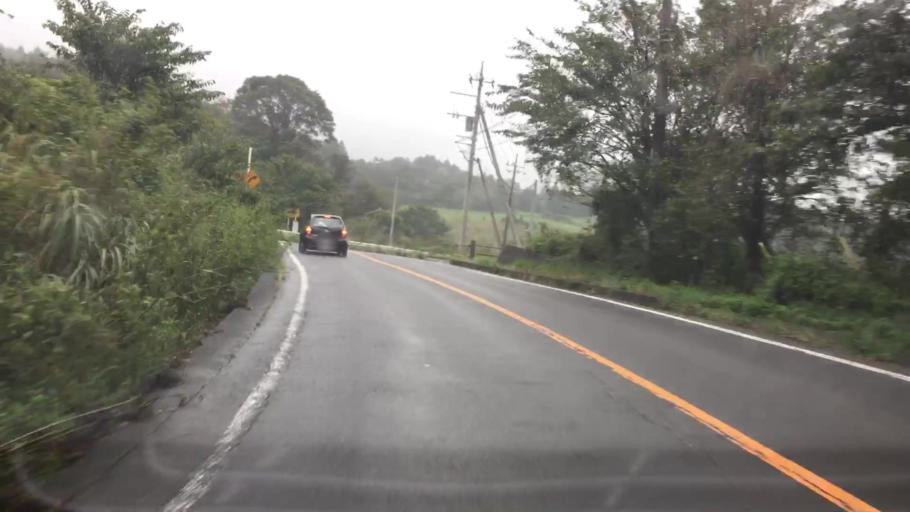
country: JP
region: Yamanashi
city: Fujikawaguchiko
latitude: 35.4046
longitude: 138.6140
